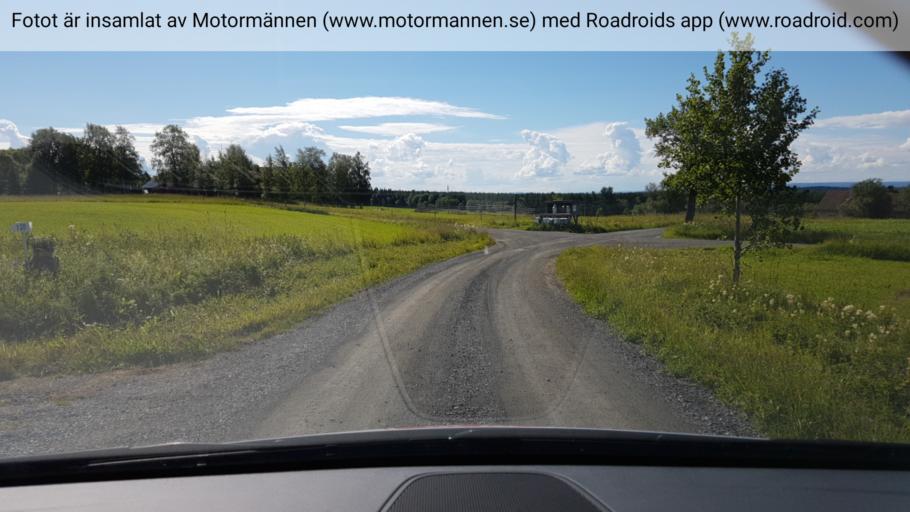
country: SE
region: Jaemtland
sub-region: OEstersunds Kommun
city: Ostersund
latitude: 63.1377
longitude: 14.4972
